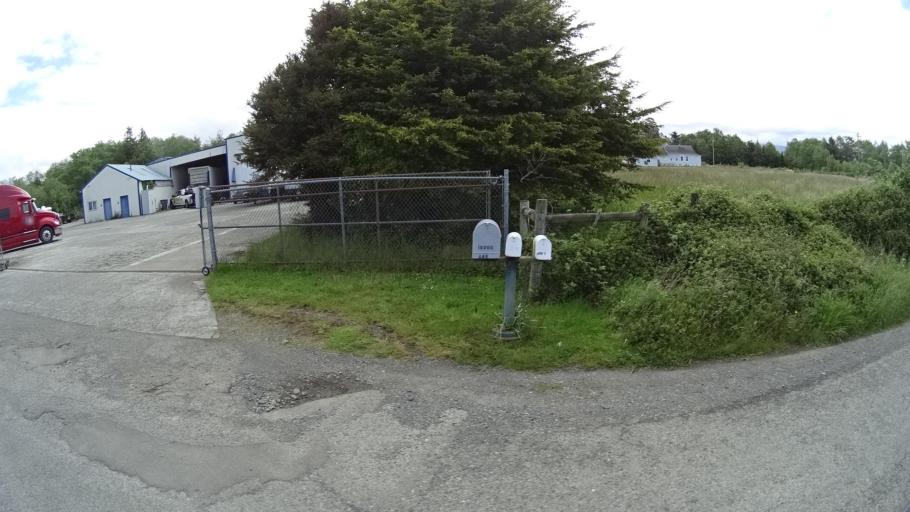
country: US
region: California
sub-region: Humboldt County
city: Arcata
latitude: 40.8784
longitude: -124.0945
